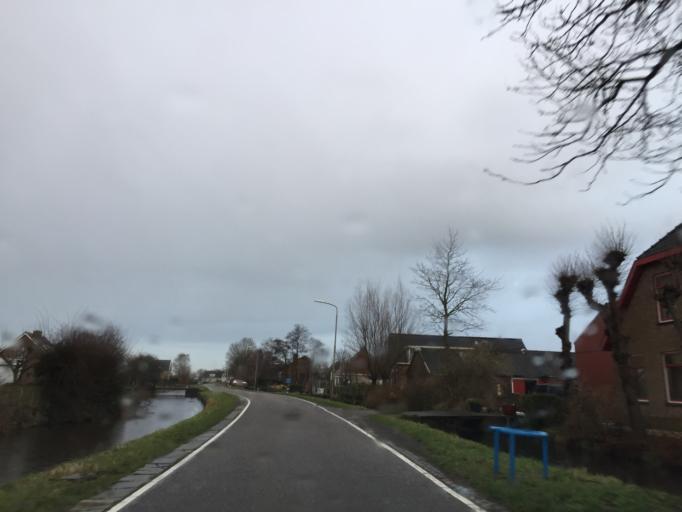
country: NL
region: South Holland
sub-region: Gemeente Pijnacker-Nootdorp
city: Pijnacker
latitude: 51.9895
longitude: 4.4297
